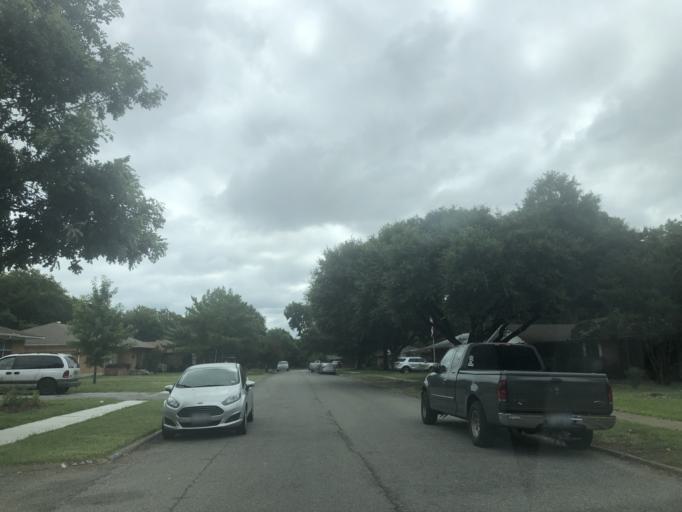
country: US
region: Texas
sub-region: Dallas County
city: Duncanville
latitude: 32.6564
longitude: -96.9124
